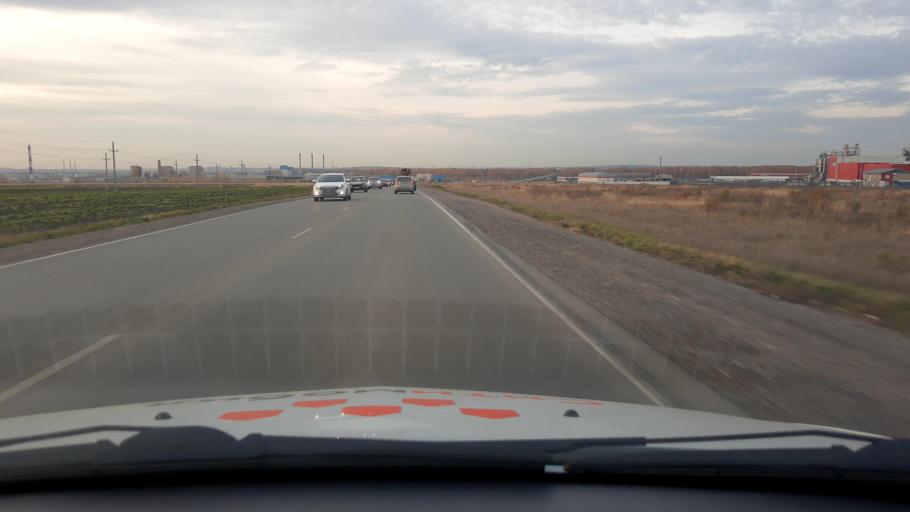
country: RU
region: Bashkortostan
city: Iglino
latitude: 54.7591
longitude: 56.2750
